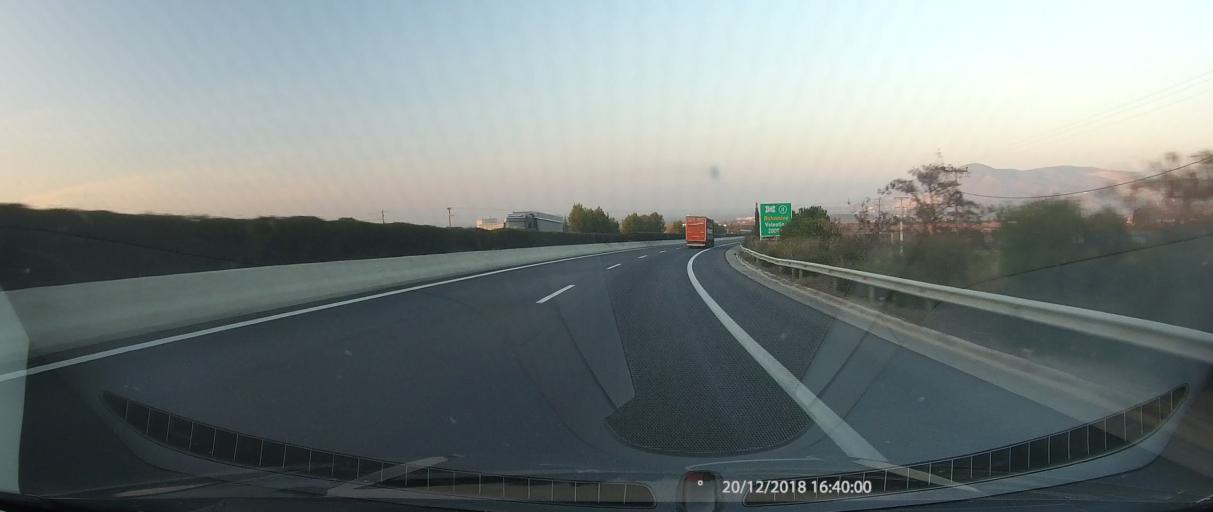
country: GR
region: Thessaly
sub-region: Nomos Magnisias
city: Velestino
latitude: 39.3669
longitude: 22.7698
